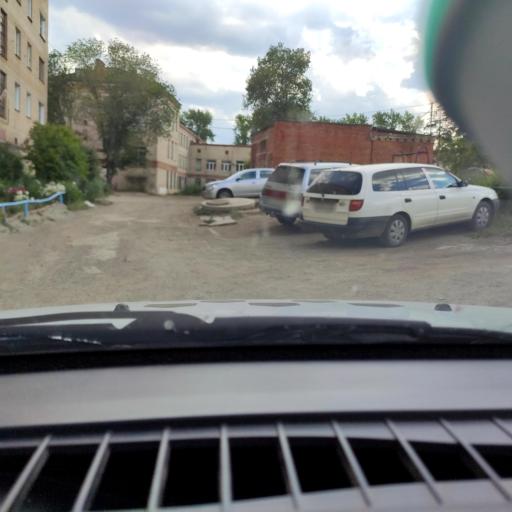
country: RU
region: Chelyabinsk
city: Miass
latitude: 55.0796
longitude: 60.0933
